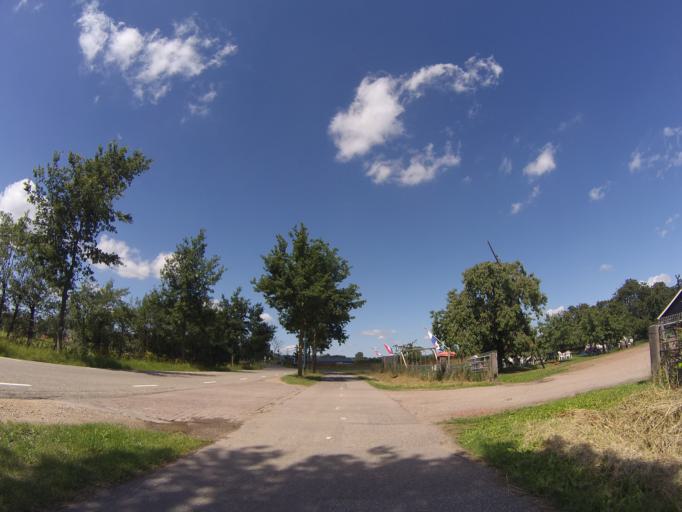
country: NL
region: Utrecht
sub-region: Stichtse Vecht
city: Spechtenkamp
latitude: 52.1173
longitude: 5.0072
